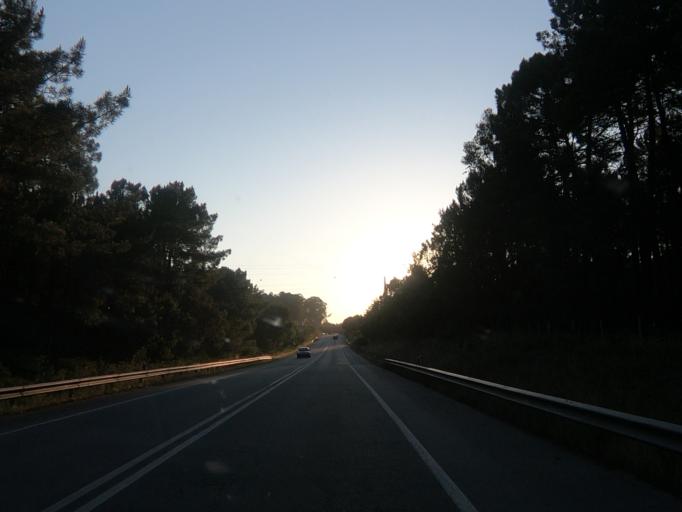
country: PT
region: Viseu
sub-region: Viseu
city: Rio de Loba
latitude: 40.6745
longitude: -7.8640
